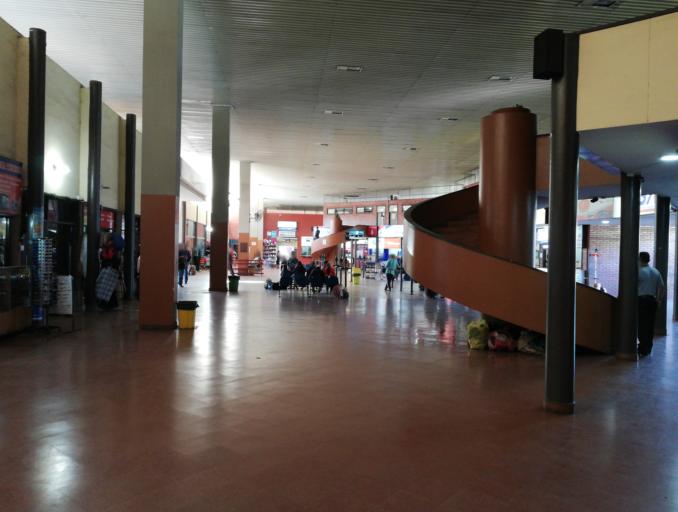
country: PY
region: Alto Parana
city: Presidente Franco
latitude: -25.5270
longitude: -54.6152
